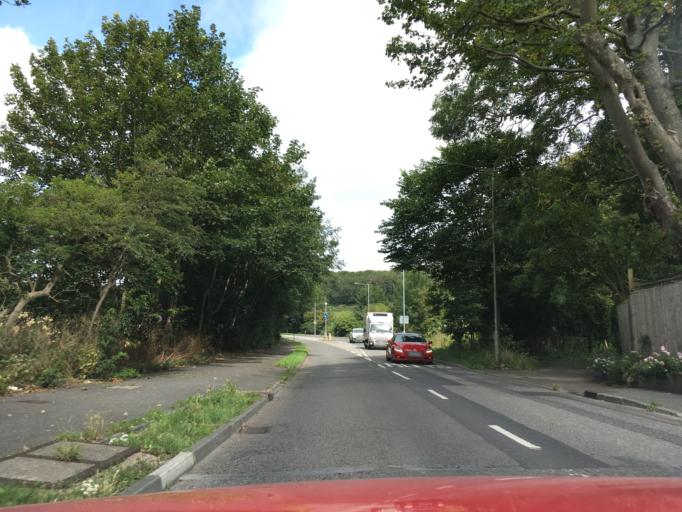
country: GB
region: England
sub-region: Brighton and Hove
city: Rottingdean
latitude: 50.8240
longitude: -0.0678
